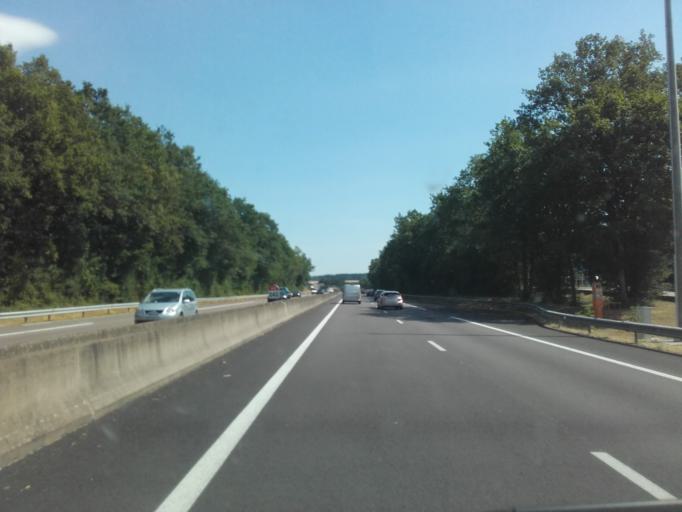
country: FR
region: Bourgogne
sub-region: Departement de la Cote-d'Or
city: Semur-en-Auxois
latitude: 47.3906
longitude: 4.3640
